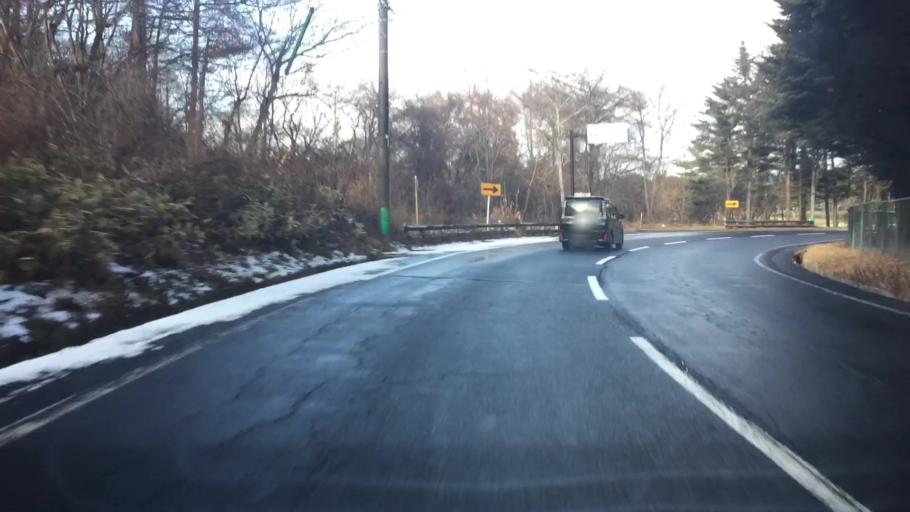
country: JP
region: Nagano
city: Saku
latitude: 36.3020
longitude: 138.6326
